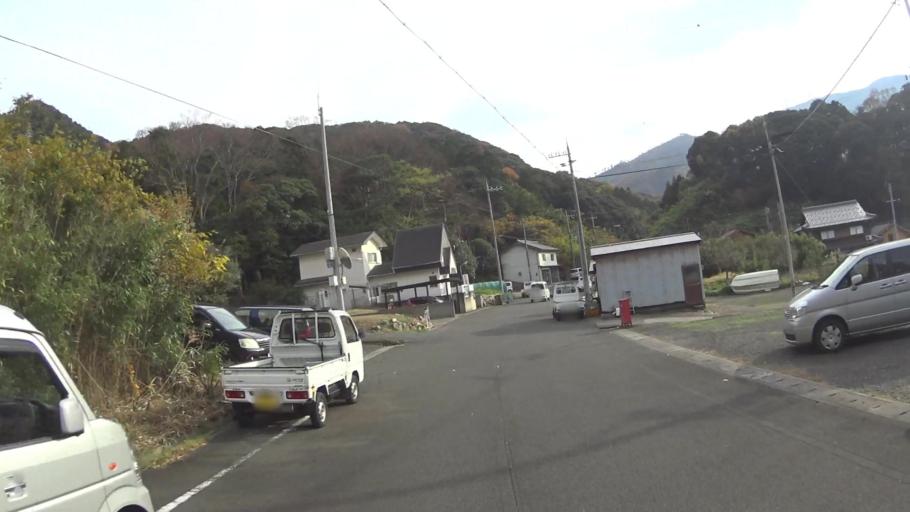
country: JP
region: Kyoto
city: Maizuru
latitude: 35.5699
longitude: 135.4299
